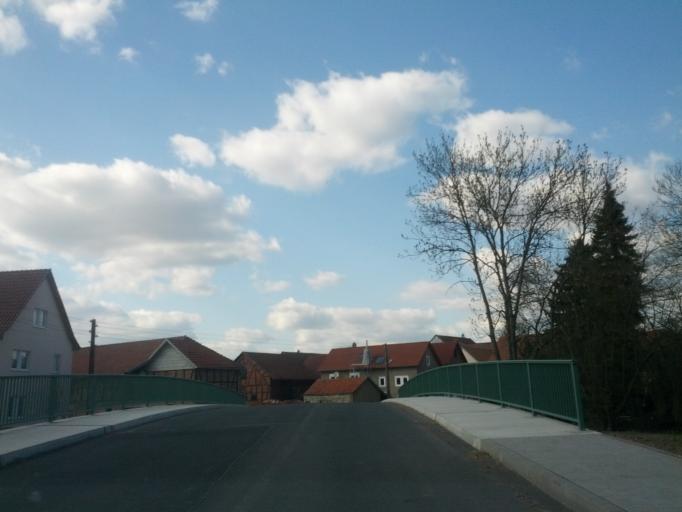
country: DE
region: Thuringia
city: Seebach
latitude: 50.9732
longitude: 10.4482
